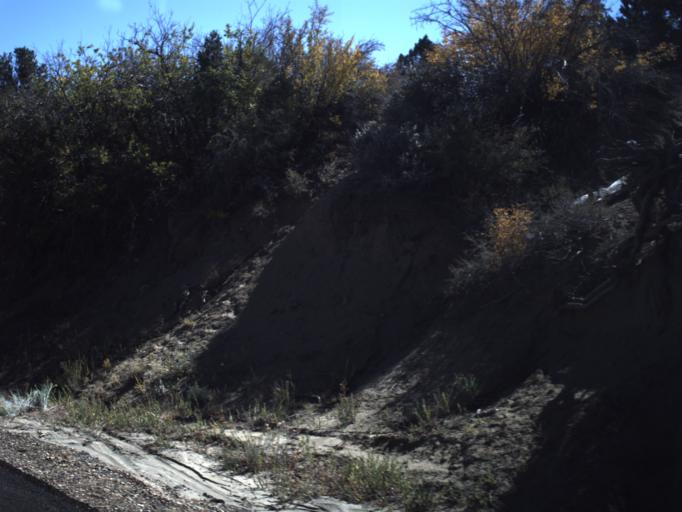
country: US
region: Utah
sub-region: Garfield County
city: Panguitch
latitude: 37.6379
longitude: -111.8433
